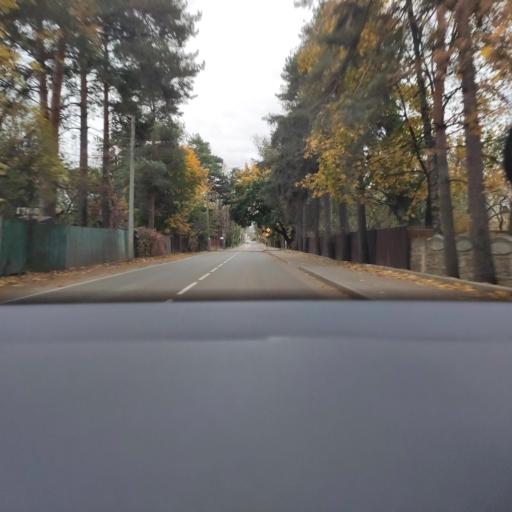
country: RU
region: Moscow
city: Mikhalkovo
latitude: 55.6697
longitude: 37.4172
